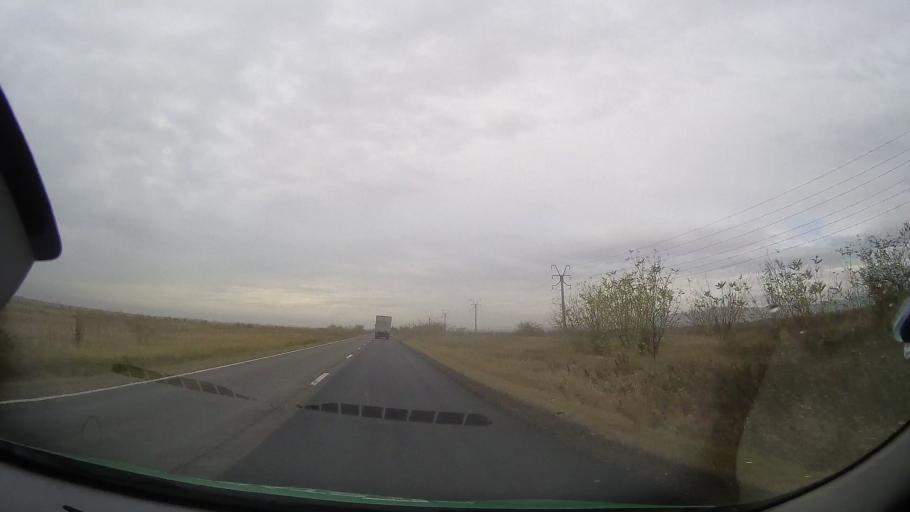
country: RO
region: Prahova
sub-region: Comuna Tomsani
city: Loloiasca
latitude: 44.9650
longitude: 26.2778
